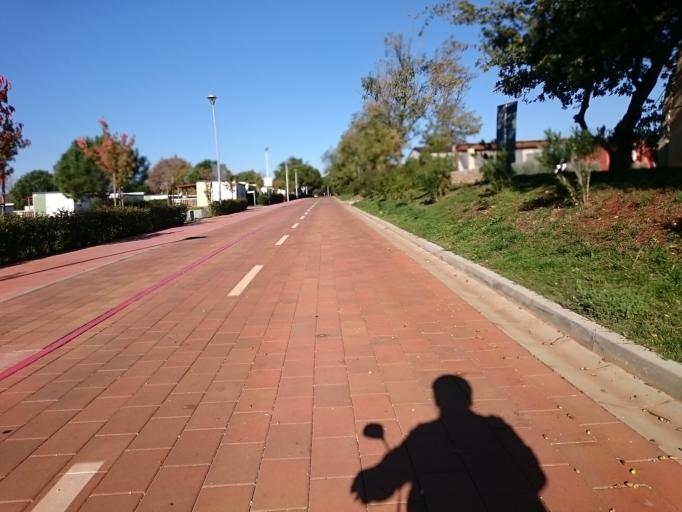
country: HR
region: Istarska
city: Novigrad
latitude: 45.3637
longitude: 13.5467
